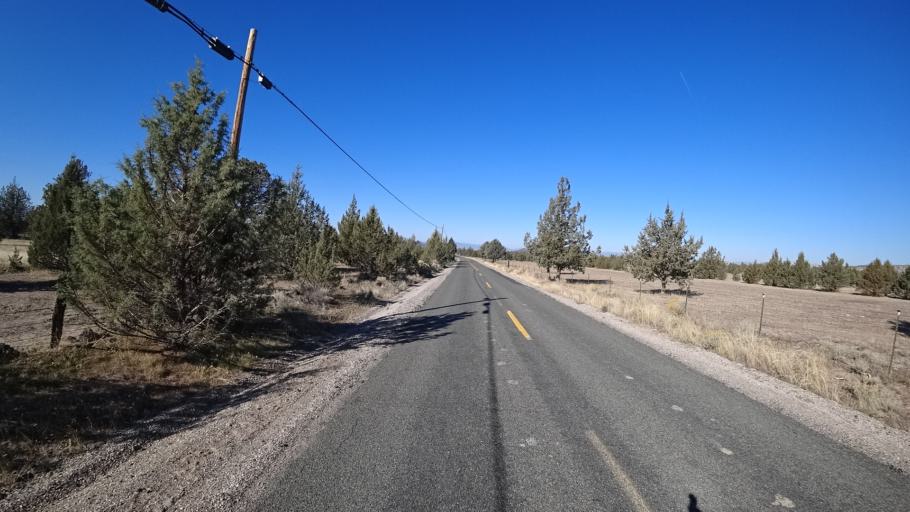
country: US
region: California
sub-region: Siskiyou County
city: Montague
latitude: 41.6420
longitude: -122.3475
